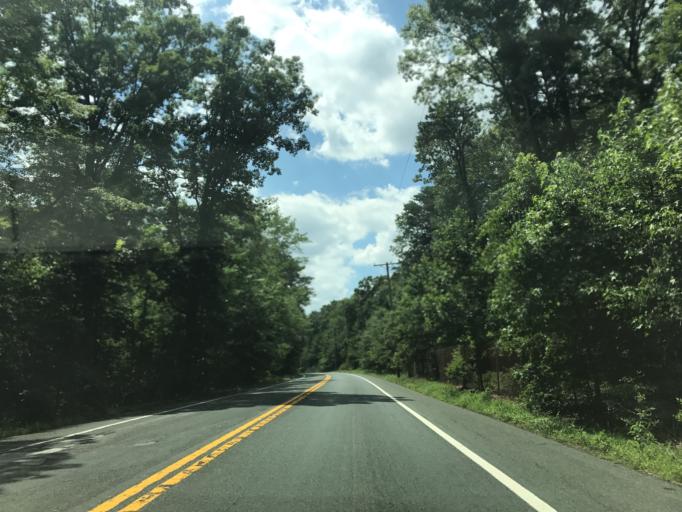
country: US
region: Maryland
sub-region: Prince George's County
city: South Laurel
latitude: 39.0477
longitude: -76.8203
